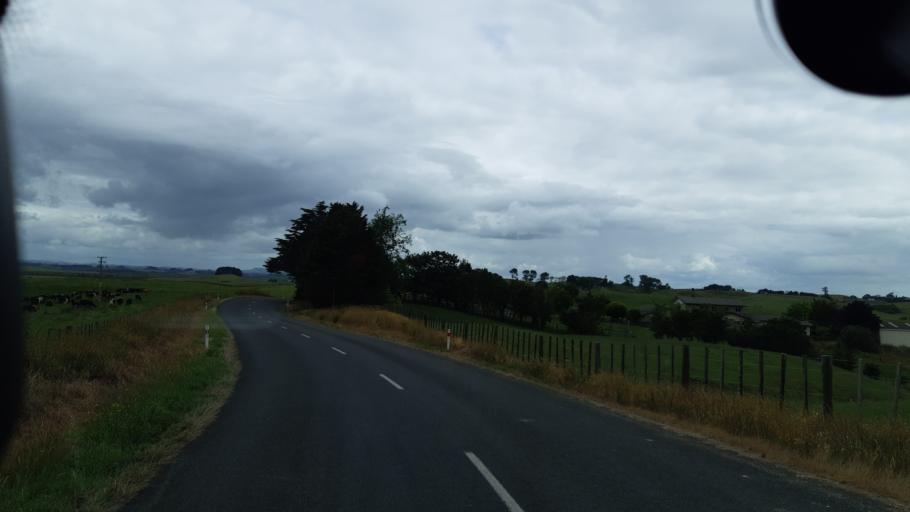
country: NZ
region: Waikato
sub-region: Waikato District
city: Te Kauwhata
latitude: -37.5029
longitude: 175.0900
